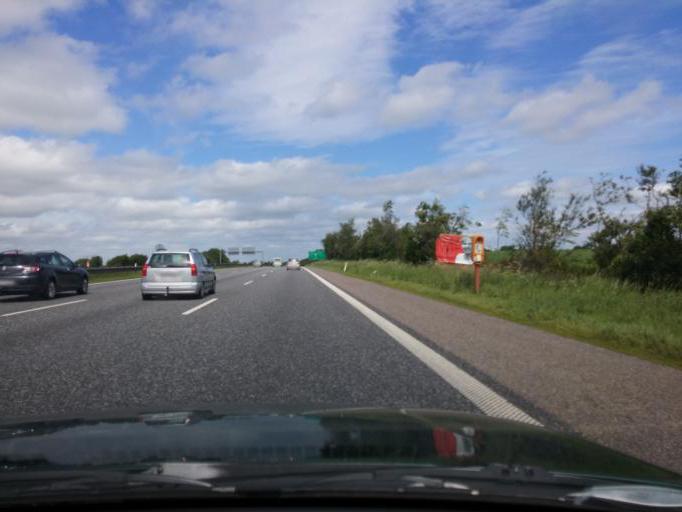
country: DK
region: South Denmark
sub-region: Kolding Kommune
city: Kolding
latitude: 55.5387
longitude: 9.5091
